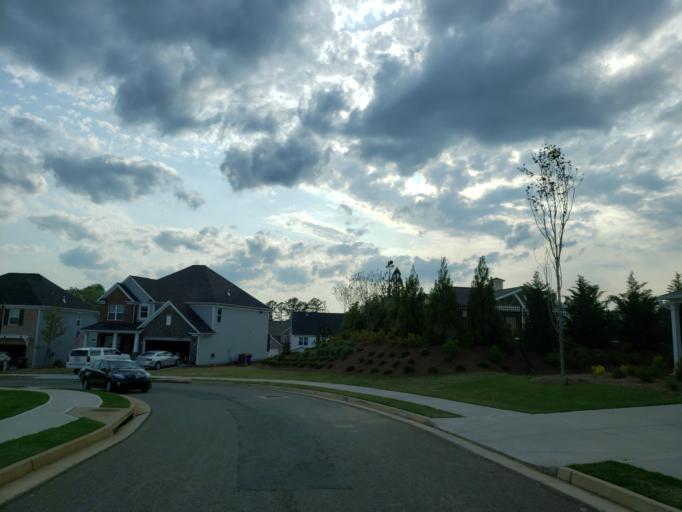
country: US
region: Georgia
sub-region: Cherokee County
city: Holly Springs
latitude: 34.1676
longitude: -84.4278
